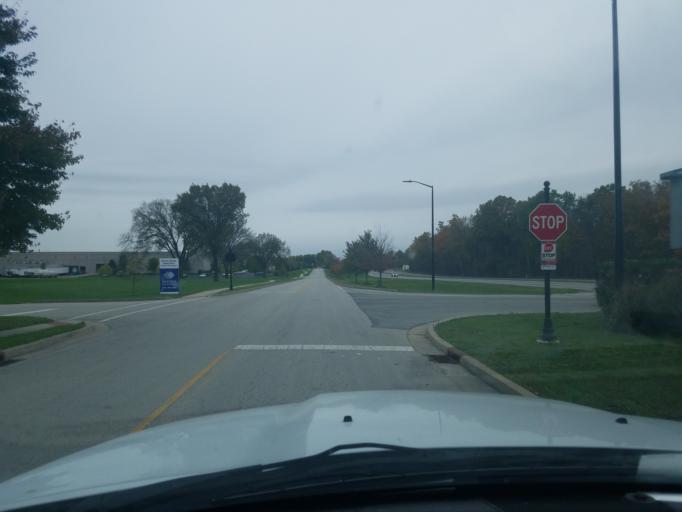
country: US
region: Indiana
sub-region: Clark County
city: Oak Park
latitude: 38.3645
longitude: -85.6986
